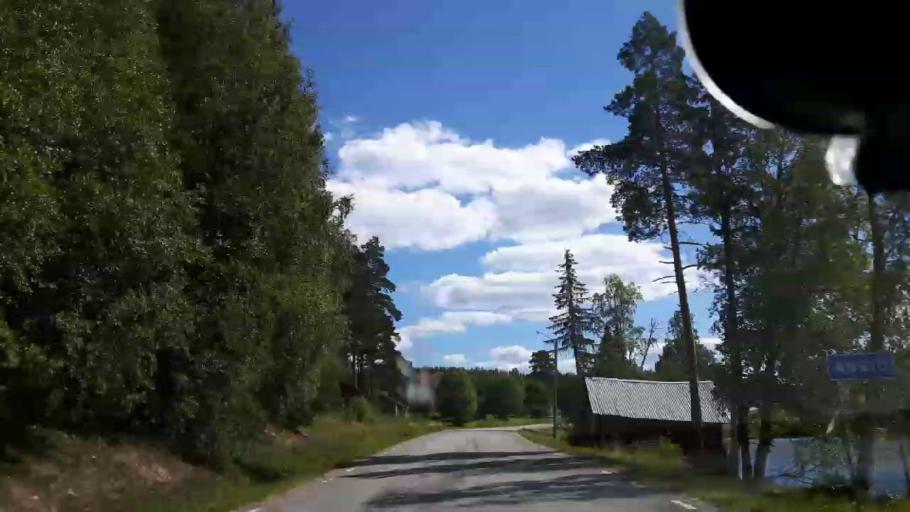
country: SE
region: Jaemtland
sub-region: Ragunda Kommun
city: Hammarstrand
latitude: 62.9663
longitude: 16.0987
